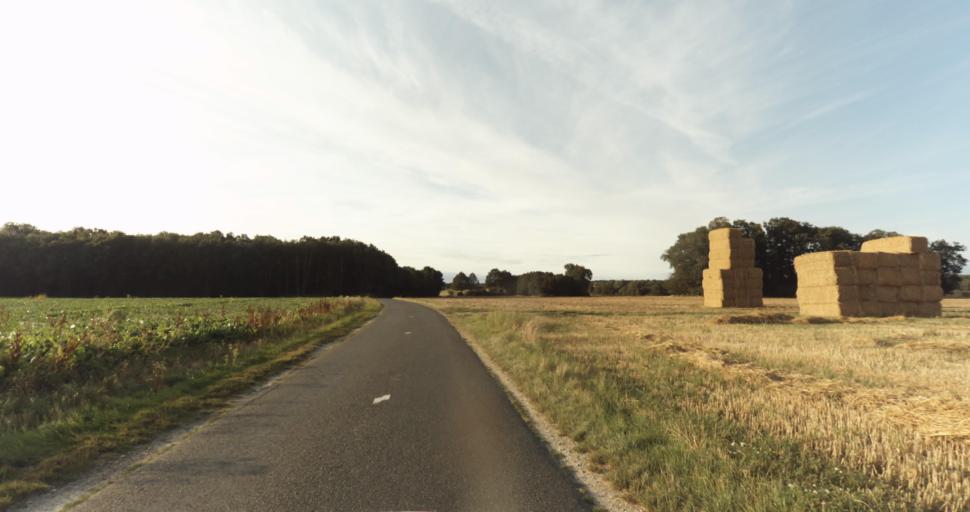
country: FR
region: Haute-Normandie
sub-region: Departement de l'Eure
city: Marcilly-sur-Eure
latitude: 48.8309
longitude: 1.2858
